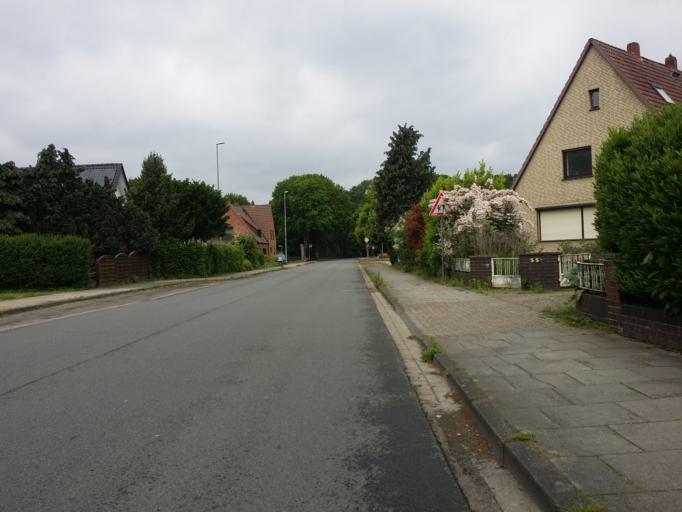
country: DE
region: Lower Saxony
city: Ganderkesee
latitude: 53.0369
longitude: 8.5349
